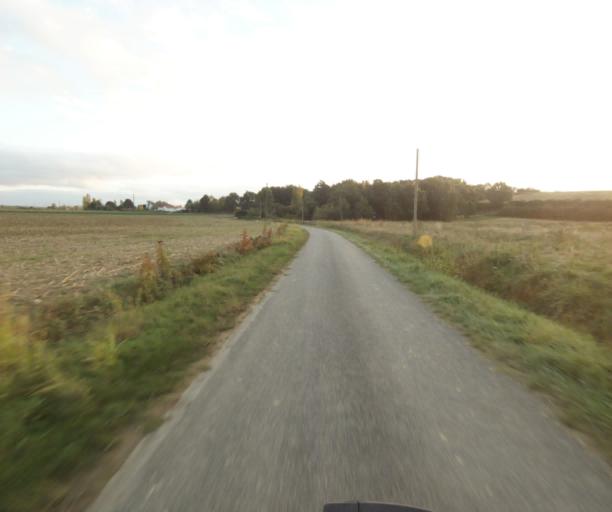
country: FR
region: Midi-Pyrenees
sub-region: Departement du Tarn-et-Garonne
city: Verdun-sur-Garonne
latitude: 43.8266
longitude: 1.2116
